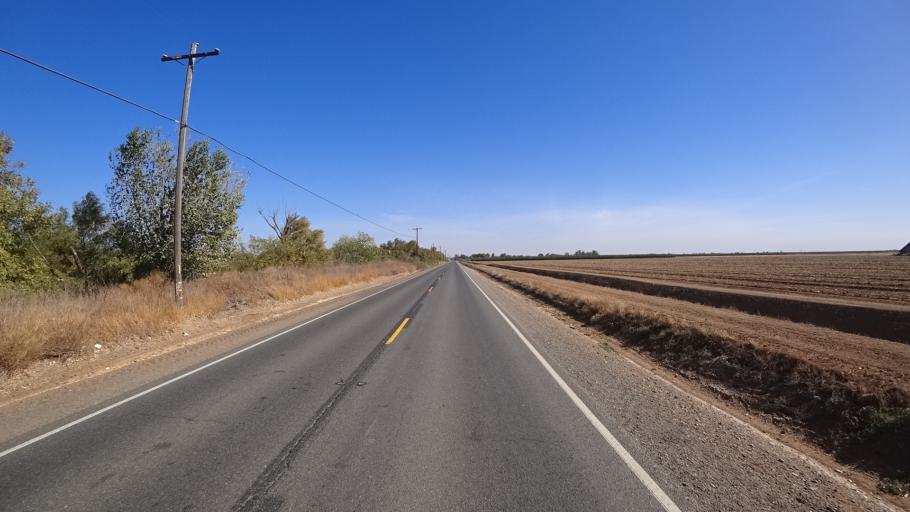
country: US
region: California
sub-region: Yolo County
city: Woodland
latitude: 38.6197
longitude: -121.8388
